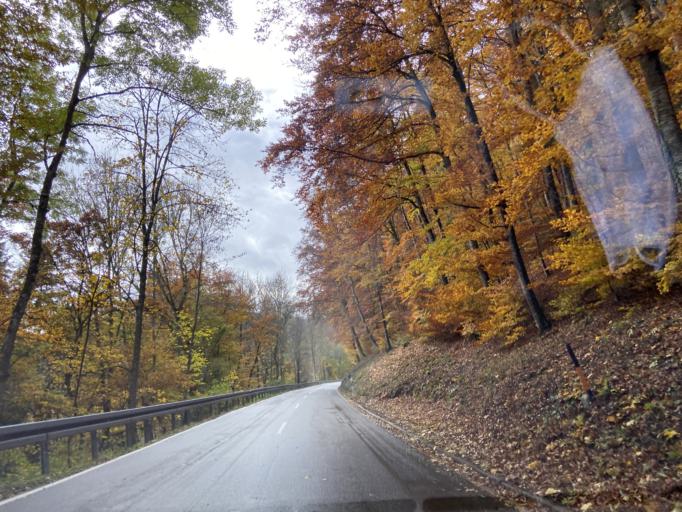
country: DE
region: Baden-Wuerttemberg
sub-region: Tuebingen Region
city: Schwenningen
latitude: 48.0869
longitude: 9.0345
